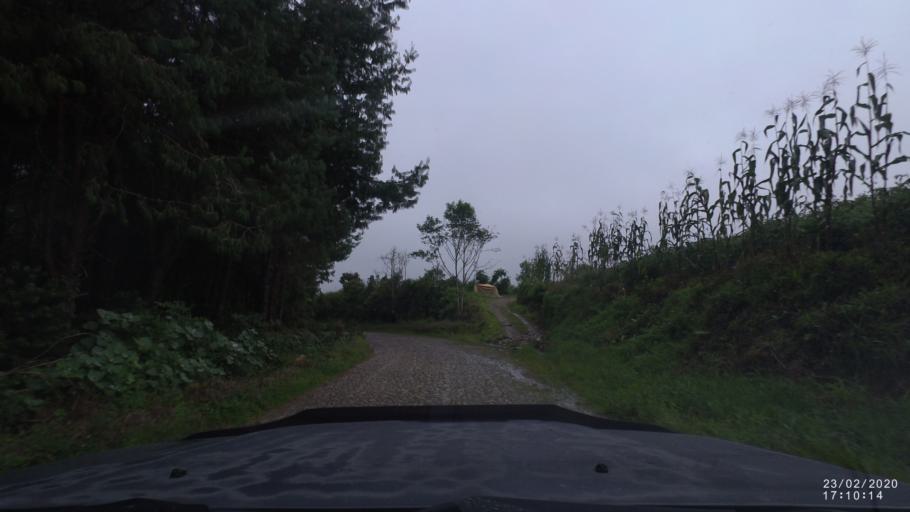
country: BO
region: Cochabamba
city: Colomi
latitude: -17.1304
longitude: -65.9489
